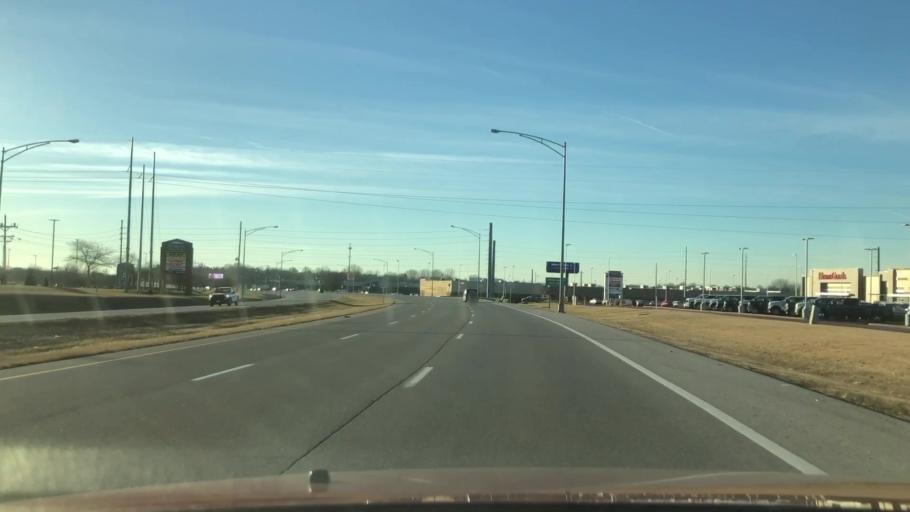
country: US
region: Missouri
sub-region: Greene County
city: Springfield
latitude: 37.1550
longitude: -93.2629
